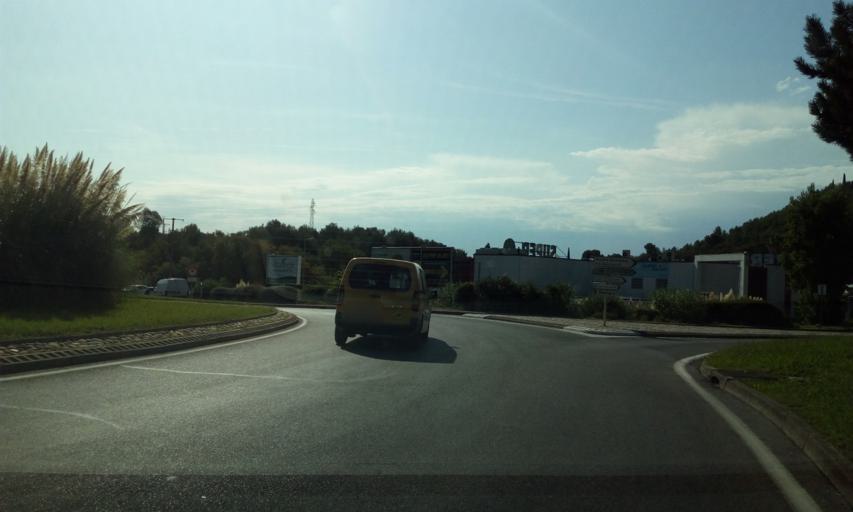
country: FR
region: Provence-Alpes-Cote d'Azur
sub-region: Departement du Var
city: Bandol
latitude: 43.1492
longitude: 5.7635
